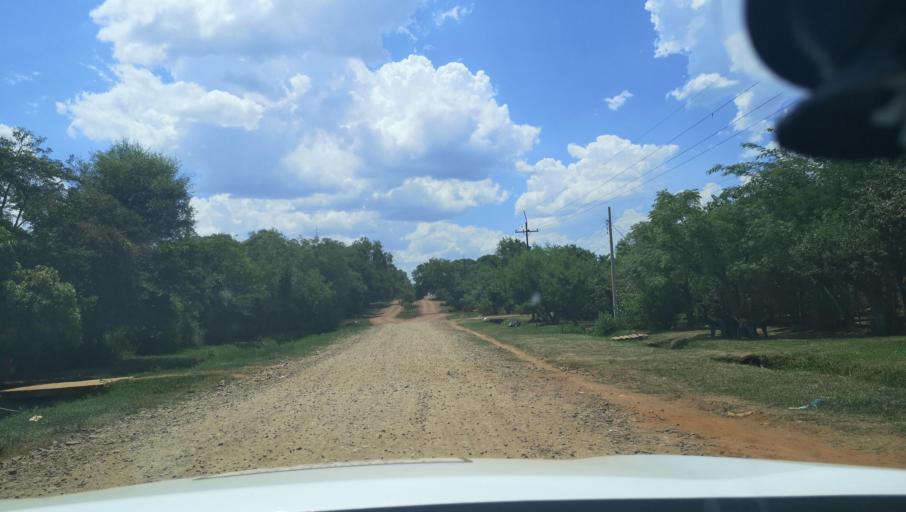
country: PY
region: Itapua
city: Carmen del Parana
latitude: -27.1691
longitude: -56.2487
